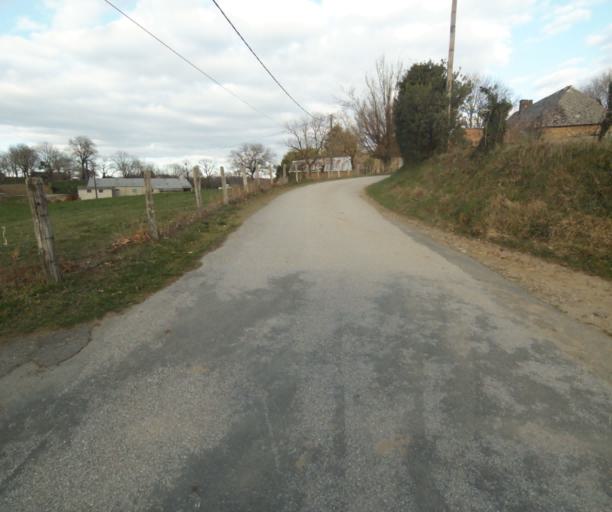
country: FR
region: Limousin
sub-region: Departement de la Correze
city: Saint-Clement
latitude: 45.3571
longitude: 1.6184
